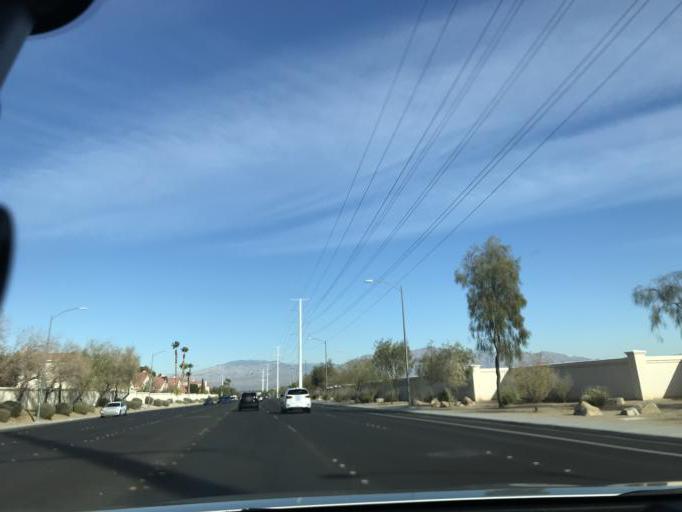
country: US
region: Nevada
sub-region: Clark County
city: Spring Valley
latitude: 36.2107
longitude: -115.2606
